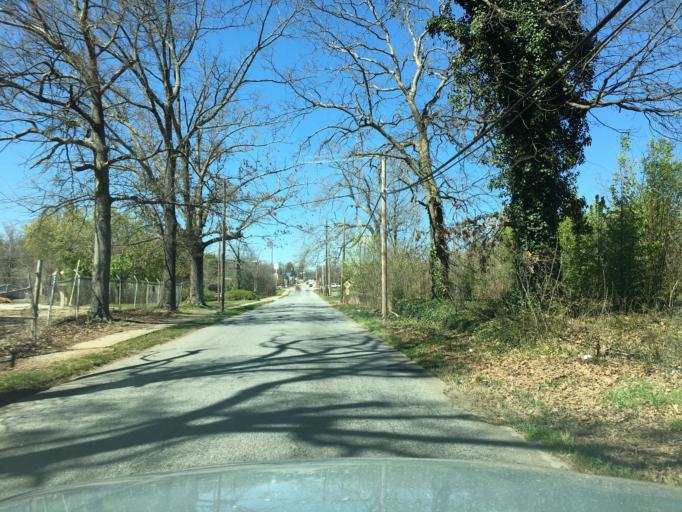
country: US
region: South Carolina
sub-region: Spartanburg County
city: Saxon
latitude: 34.9618
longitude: -81.9676
